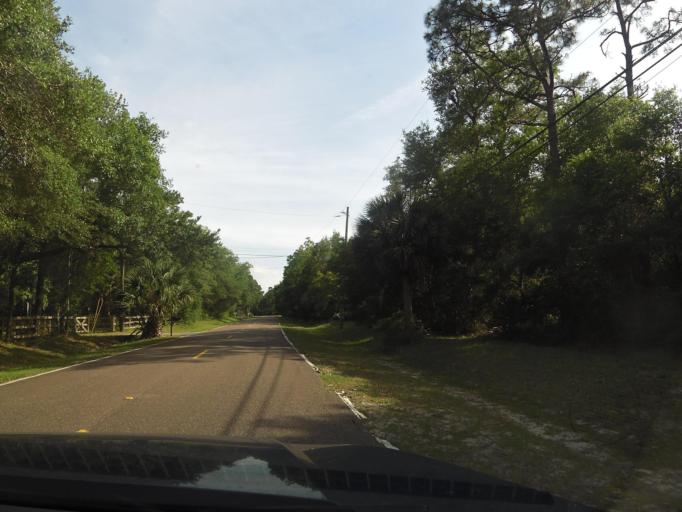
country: US
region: Florida
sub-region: Duval County
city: Atlantic Beach
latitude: 30.4647
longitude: -81.4863
